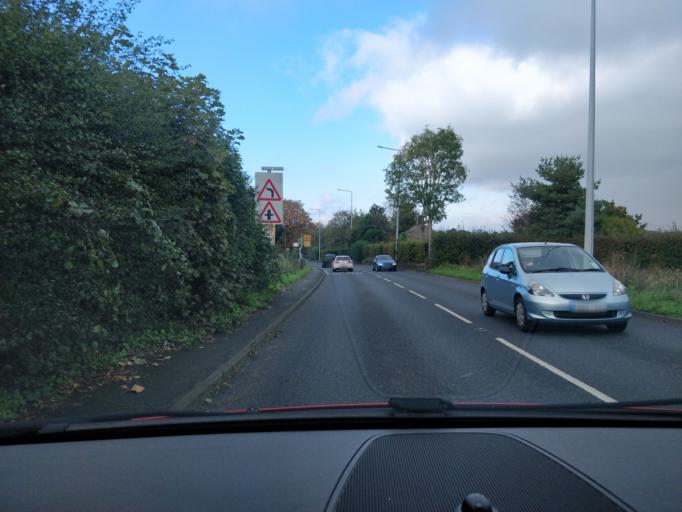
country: GB
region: England
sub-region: Lancashire
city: Ormskirk
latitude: 53.5949
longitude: -2.9218
